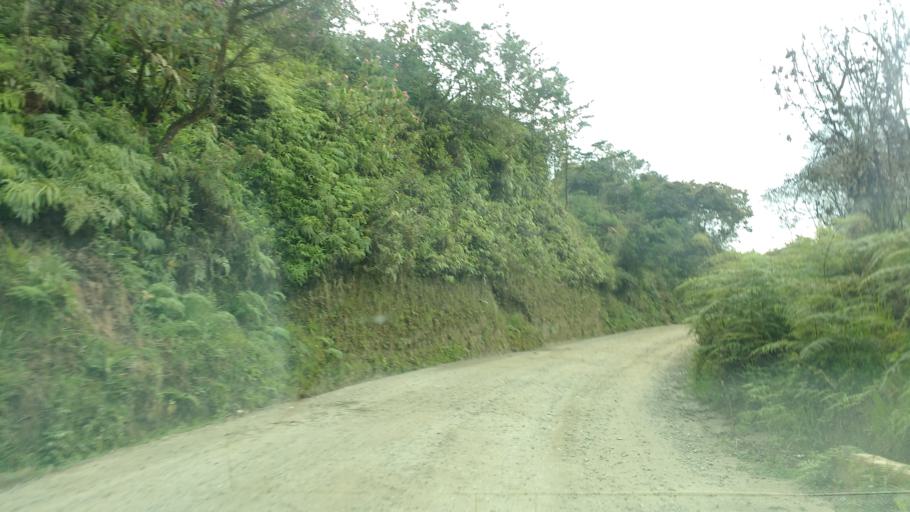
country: CO
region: Antioquia
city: San Vicente
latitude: 6.3134
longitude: -75.3134
